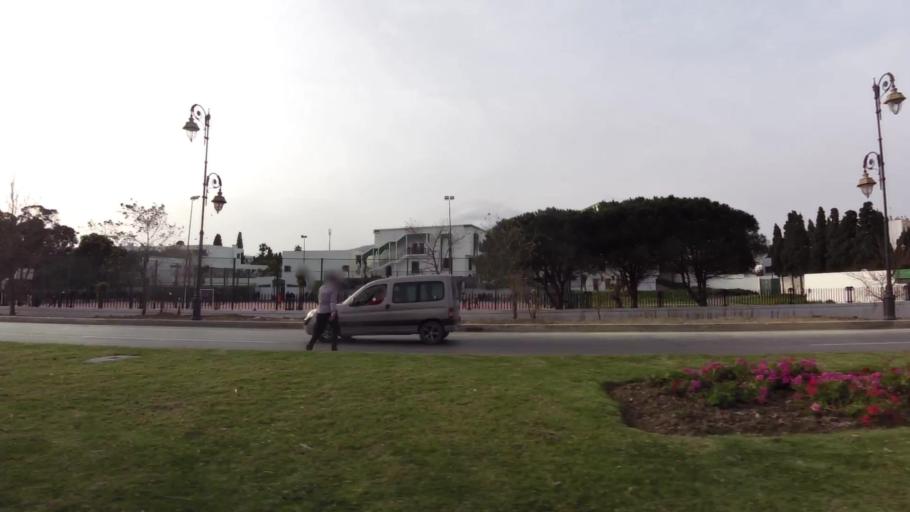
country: MA
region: Tanger-Tetouan
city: Tetouan
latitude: 35.5613
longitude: -5.3612
